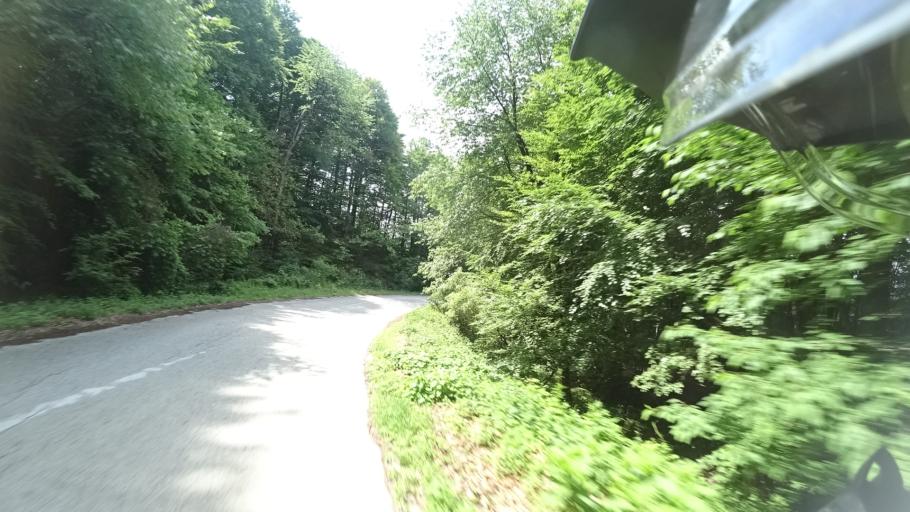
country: HR
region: Sisacko-Moslavacka
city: Gvozd
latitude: 45.3095
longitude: 15.8051
